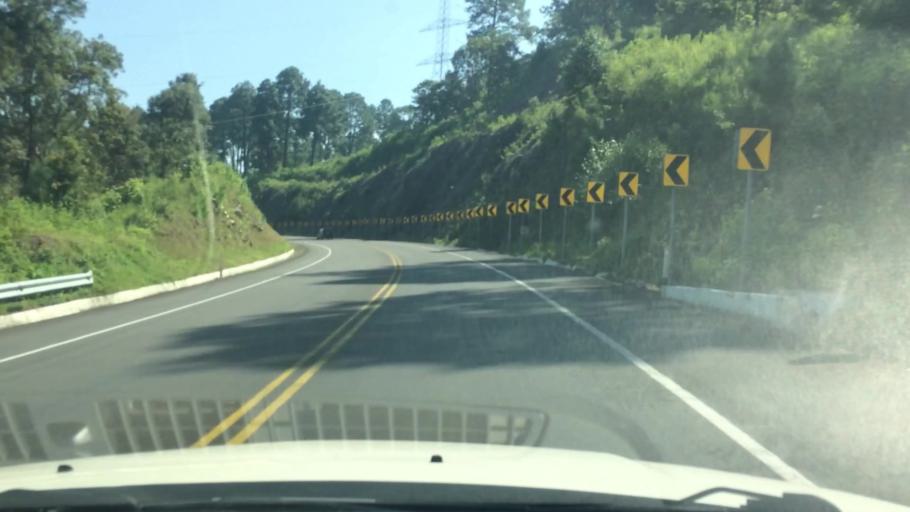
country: MX
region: Mexico
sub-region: Amanalco
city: Polvillos (San Bartolo Quinta Seccion)
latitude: 19.2200
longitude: -100.0886
